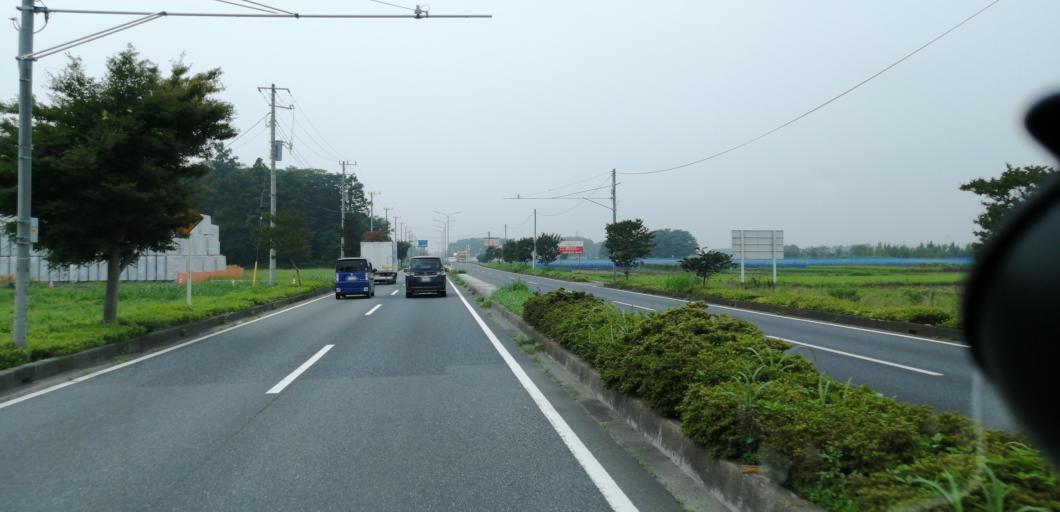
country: JP
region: Saitama
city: Fukayacho
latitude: 36.1475
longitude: 139.2695
